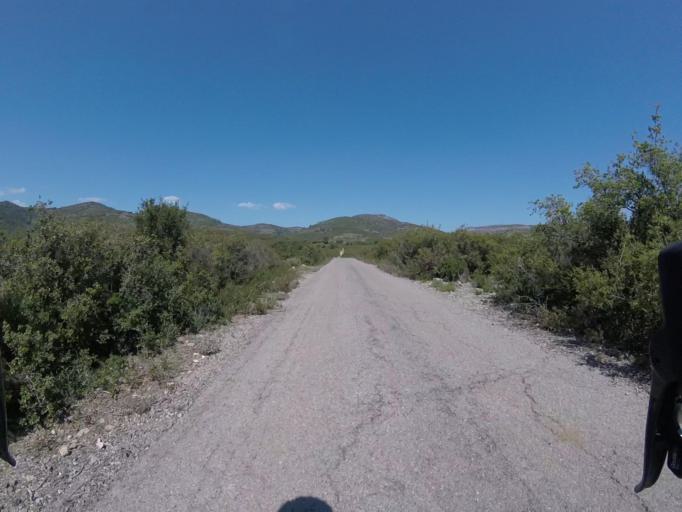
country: ES
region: Valencia
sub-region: Provincia de Castello
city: Sierra-Engarceran
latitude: 40.2439
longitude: -0.0270
